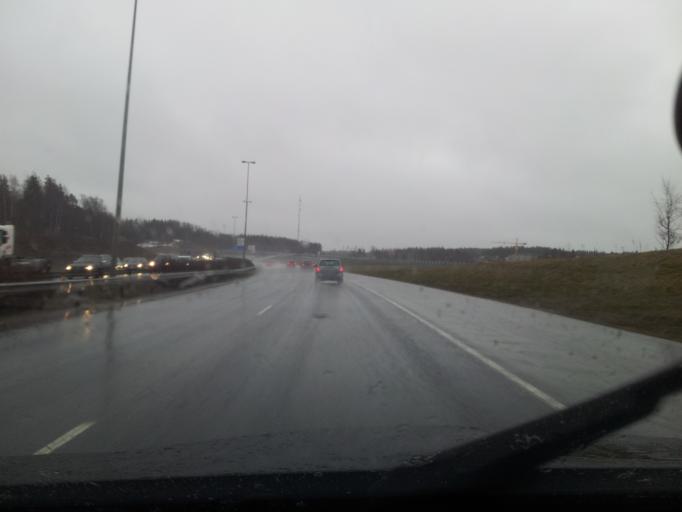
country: FI
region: Uusimaa
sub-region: Helsinki
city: Kauniainen
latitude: 60.1932
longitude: 24.7437
